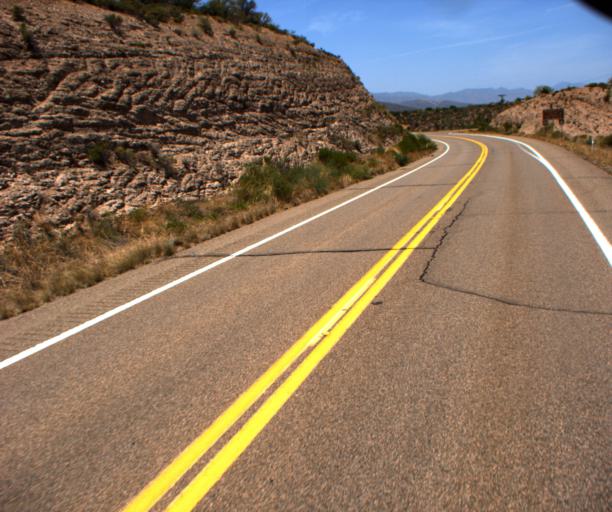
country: US
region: Arizona
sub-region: Gila County
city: Tonto Basin
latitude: 33.6658
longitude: -111.1283
